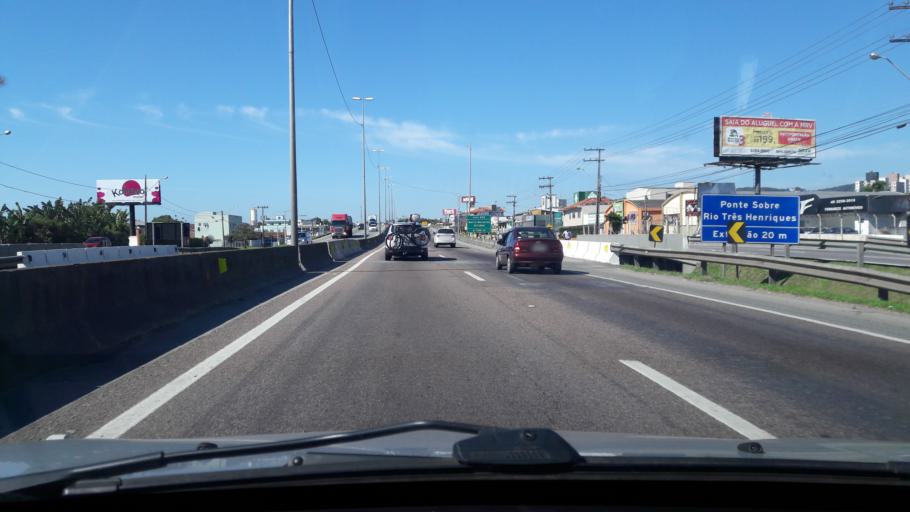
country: BR
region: Santa Catarina
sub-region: Sao Jose
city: Campinas
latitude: -27.5502
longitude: -48.6196
